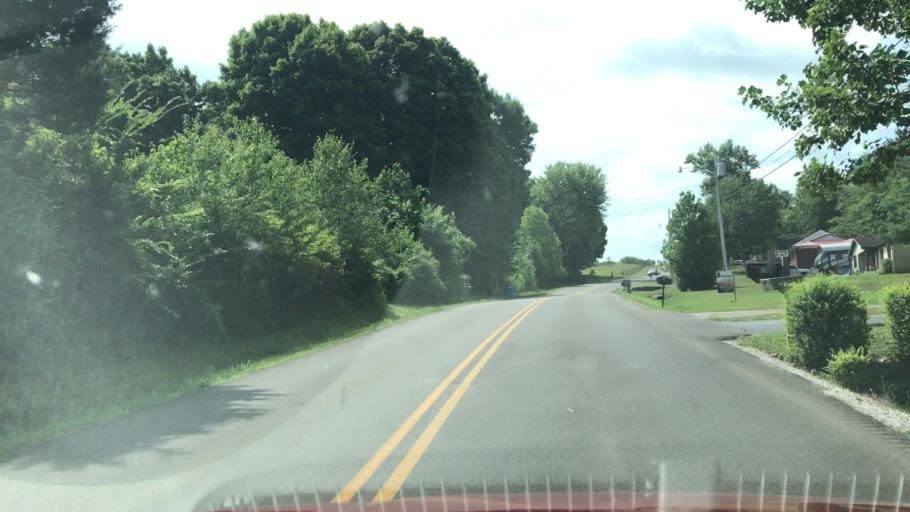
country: US
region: Kentucky
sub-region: Barren County
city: Glasgow
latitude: 36.9846
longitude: -85.9041
